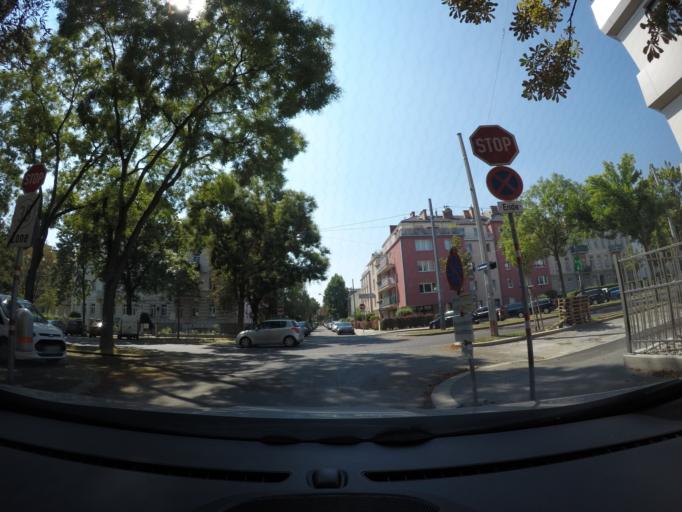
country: AT
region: Lower Austria
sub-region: Politischer Bezirk Modling
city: Perchtoldsdorf
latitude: 48.1878
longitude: 16.2798
